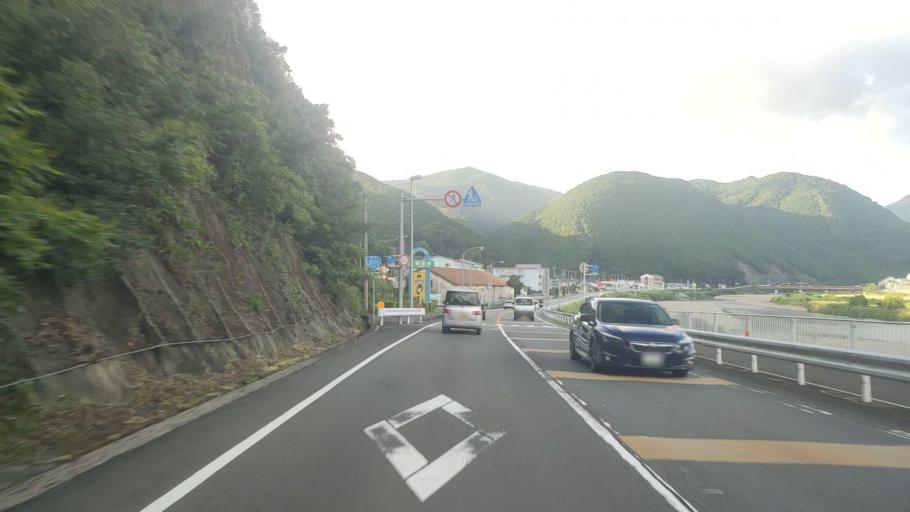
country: JP
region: Wakayama
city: Tanabe
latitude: 33.7239
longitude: 135.4813
